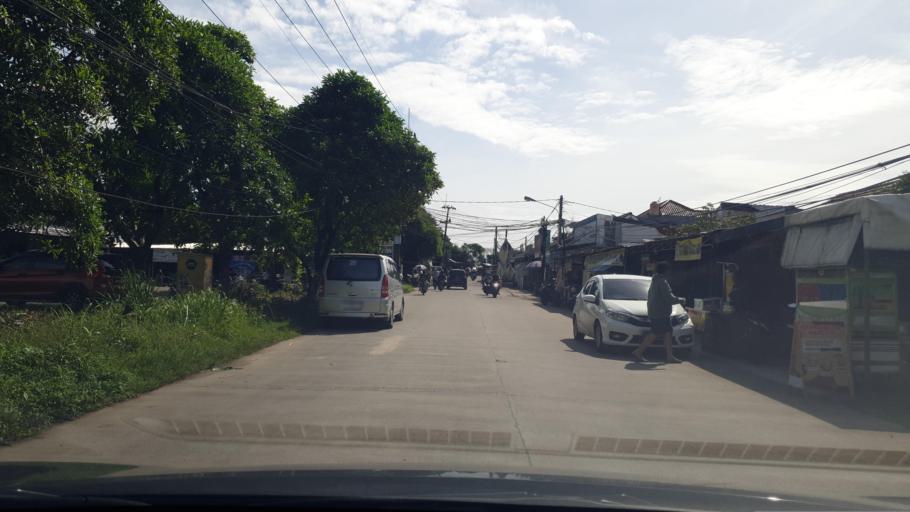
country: ID
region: West Java
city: Sawangan
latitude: -6.4067
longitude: 106.7769
